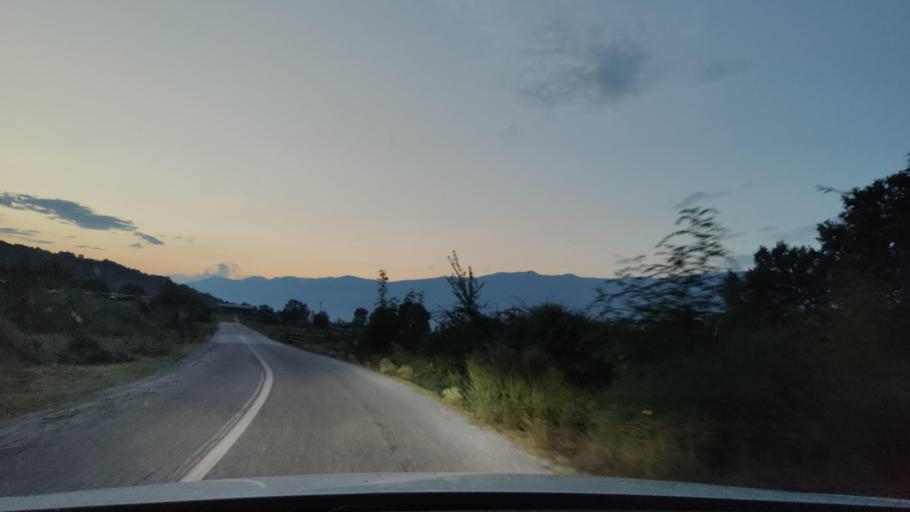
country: GR
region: Central Macedonia
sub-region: Nomos Serron
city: Chrysochorafa
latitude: 41.2037
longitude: 23.0771
